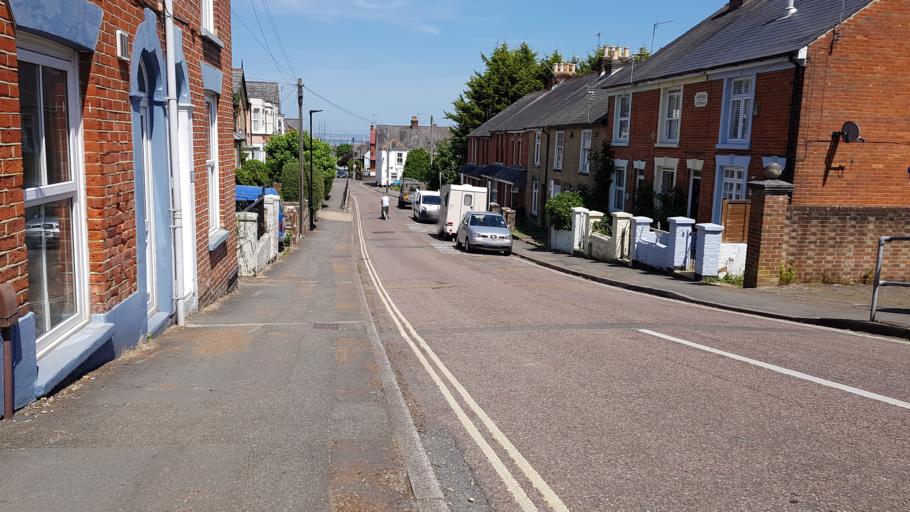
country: GB
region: England
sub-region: Isle of Wight
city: Cowes
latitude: 50.7593
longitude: -1.3019
